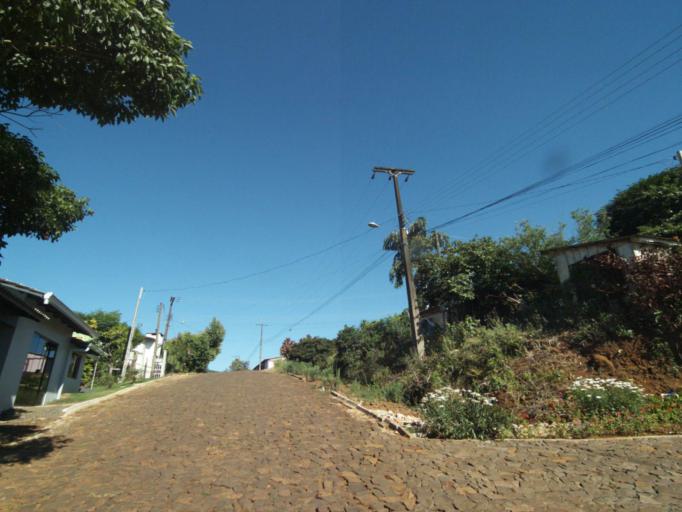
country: BR
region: Parana
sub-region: Ampere
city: Ampere
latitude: -26.1694
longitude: -53.3672
